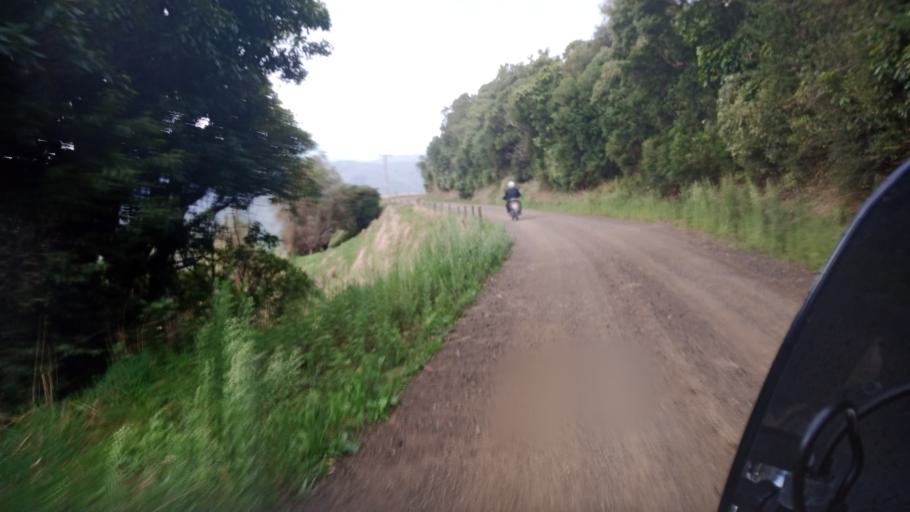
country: NZ
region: Gisborne
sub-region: Gisborne District
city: Gisborne
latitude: -38.4781
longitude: 177.6109
